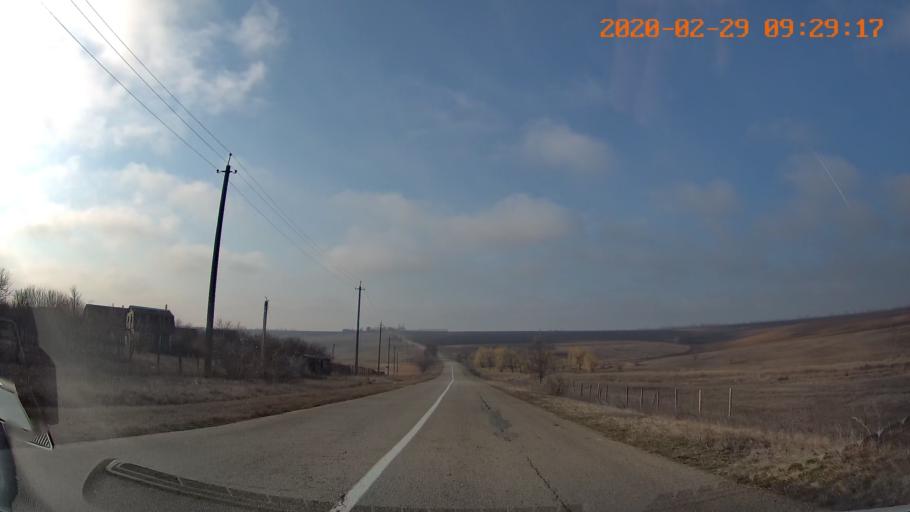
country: UA
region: Odessa
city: Lymanske
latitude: 46.6804
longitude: 29.9226
